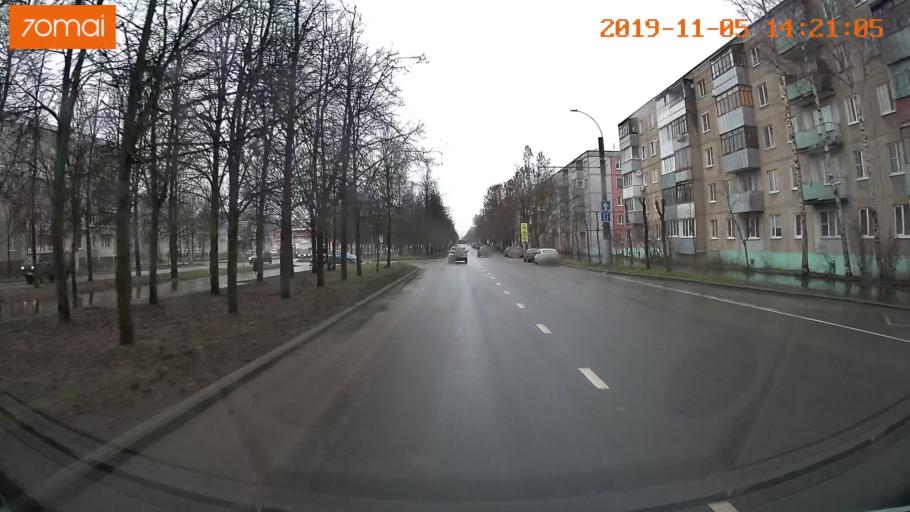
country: RU
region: Ivanovo
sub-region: Gorod Ivanovo
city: Ivanovo
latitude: 56.9571
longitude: 41.0137
